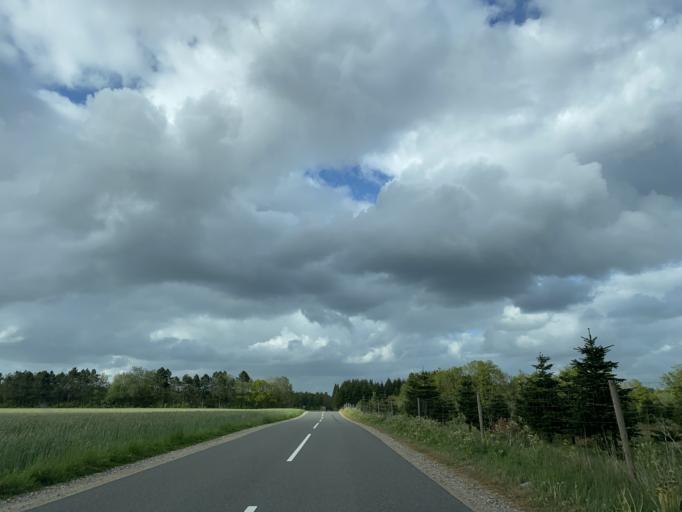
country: DK
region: Central Jutland
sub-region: Horsens Kommune
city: Braedstrup
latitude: 56.0392
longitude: 9.6634
